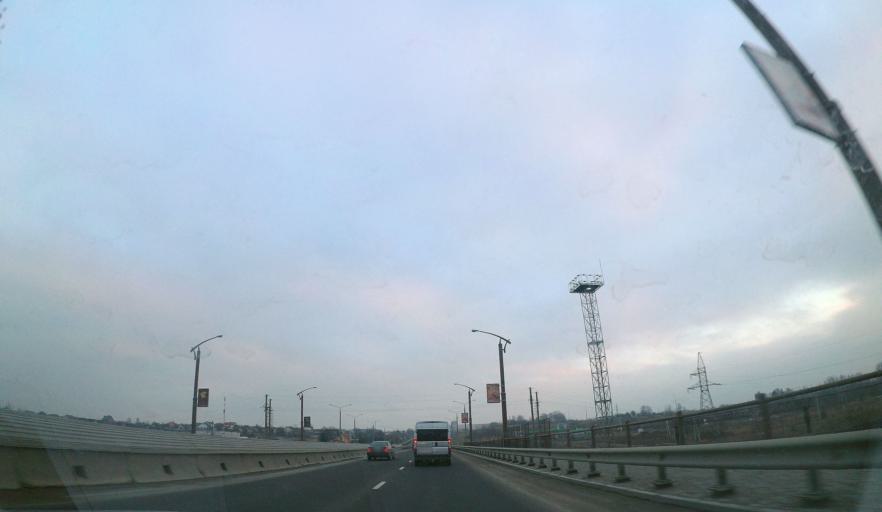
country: BY
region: Grodnenskaya
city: Hrodna
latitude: 53.6508
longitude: 23.8003
